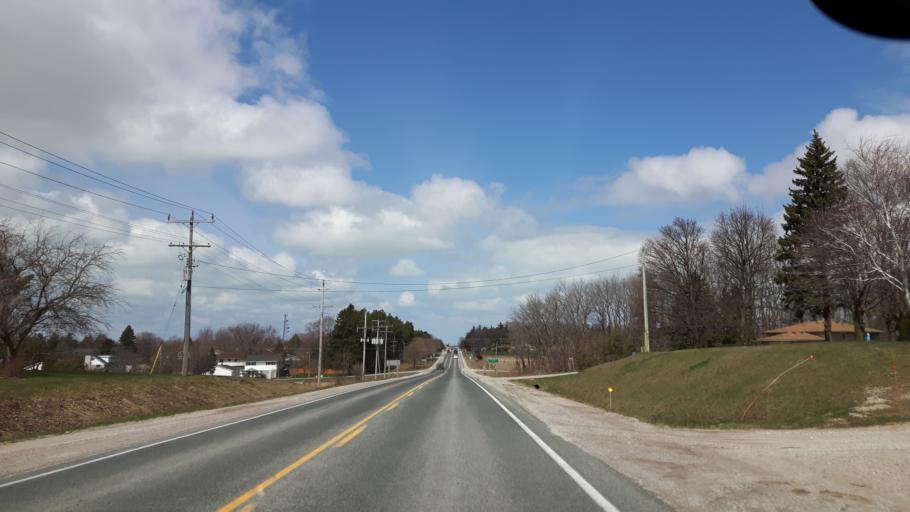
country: CA
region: Ontario
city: Goderich
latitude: 43.7228
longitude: -81.6785
